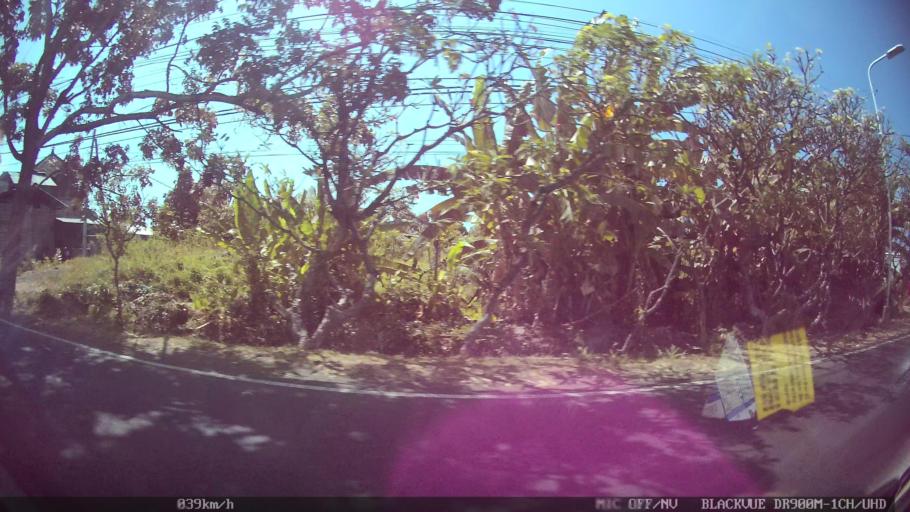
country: ID
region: Bali
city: Pegayaman
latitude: -8.1832
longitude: 114.9861
